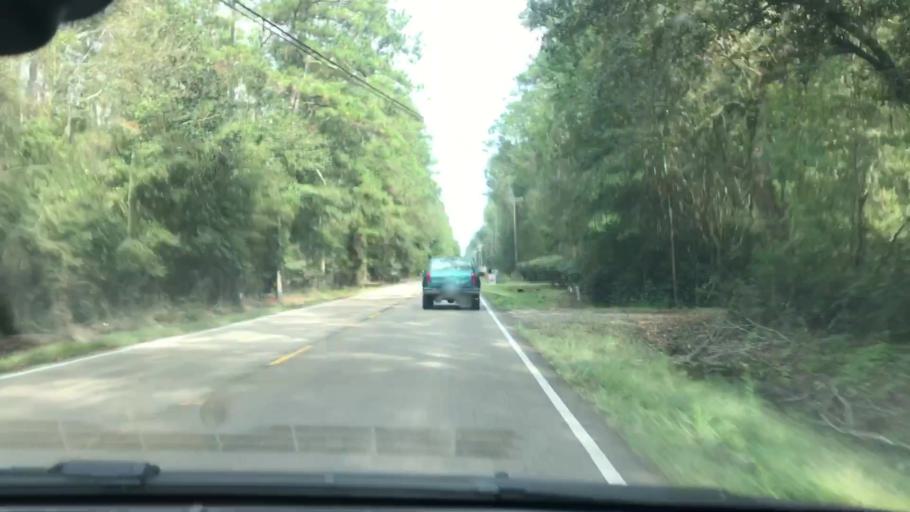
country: US
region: Louisiana
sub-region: Saint Tammany Parish
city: Abita Springs
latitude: 30.4932
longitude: -90.0116
